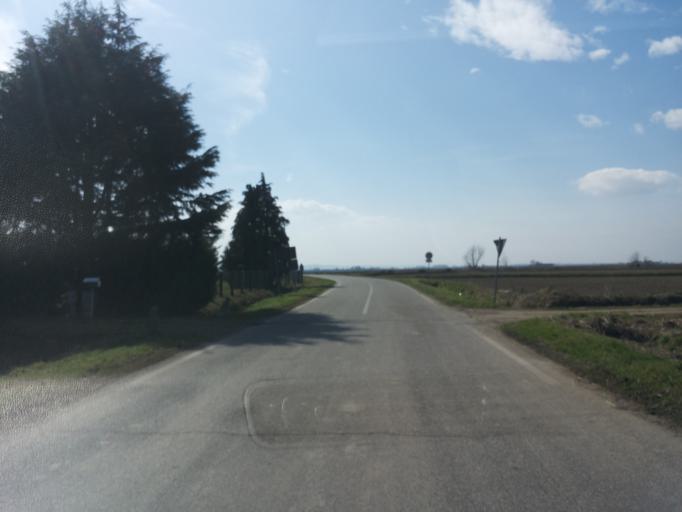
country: IT
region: Piedmont
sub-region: Provincia di Vercelli
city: Asigliano Vercellese
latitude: 45.2575
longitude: 8.4000
